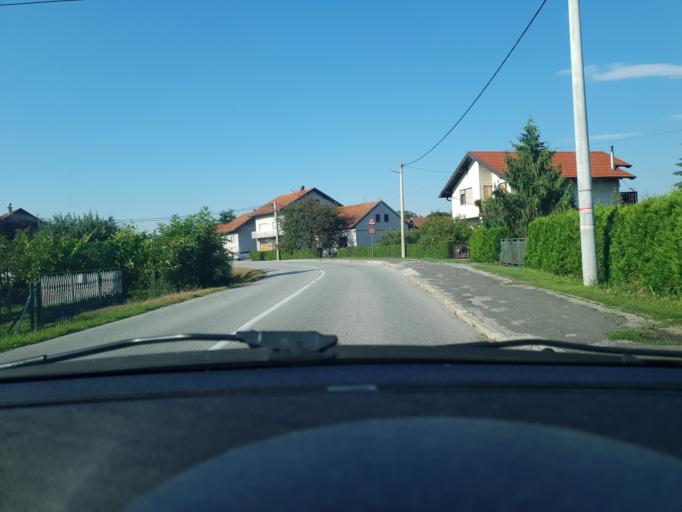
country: HR
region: Krapinsko-Zagorska
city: Oroslavje
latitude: 45.9896
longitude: 15.9176
